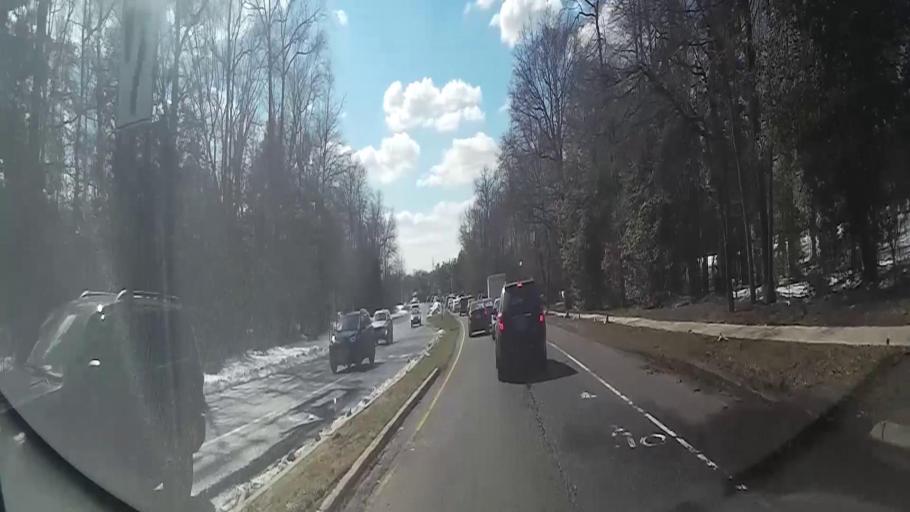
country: US
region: New Jersey
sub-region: Burlington County
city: Marlton
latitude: 39.8755
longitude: -74.9188
